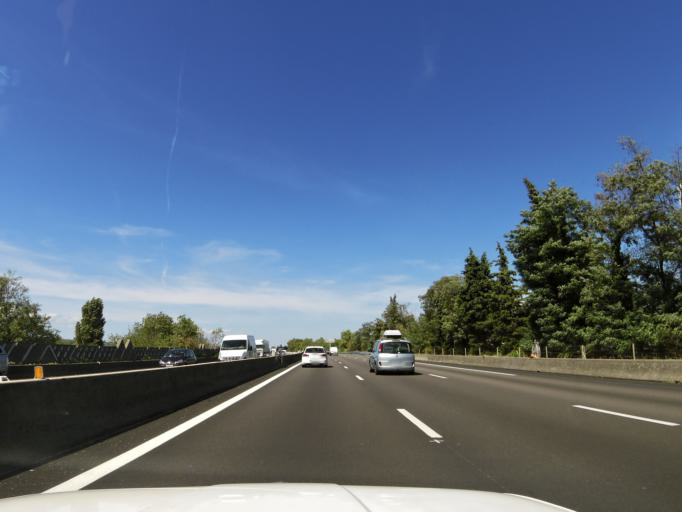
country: FR
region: Rhone-Alpes
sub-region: Departement de la Drome
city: Bourg-les-Valence
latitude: 44.9590
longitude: 4.8870
